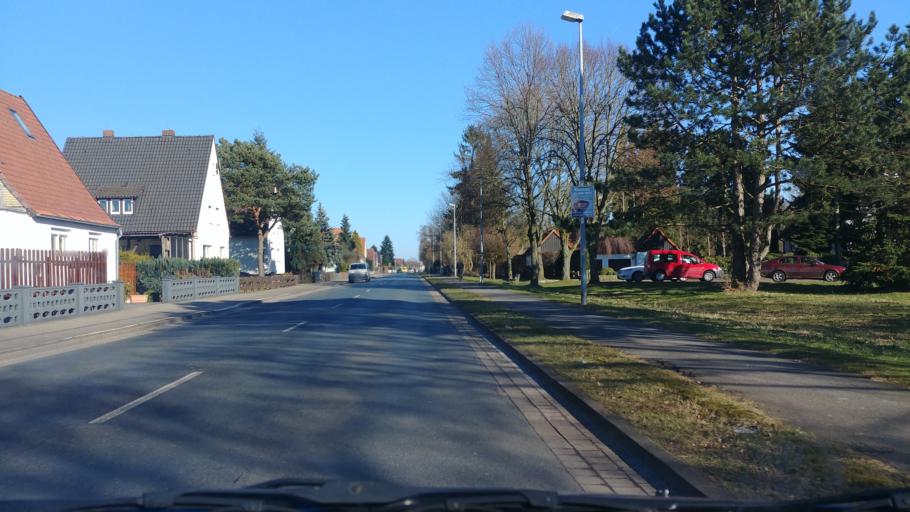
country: DE
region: Lower Saxony
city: Neustadt am Rubenberge
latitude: 52.5043
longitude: 9.4345
